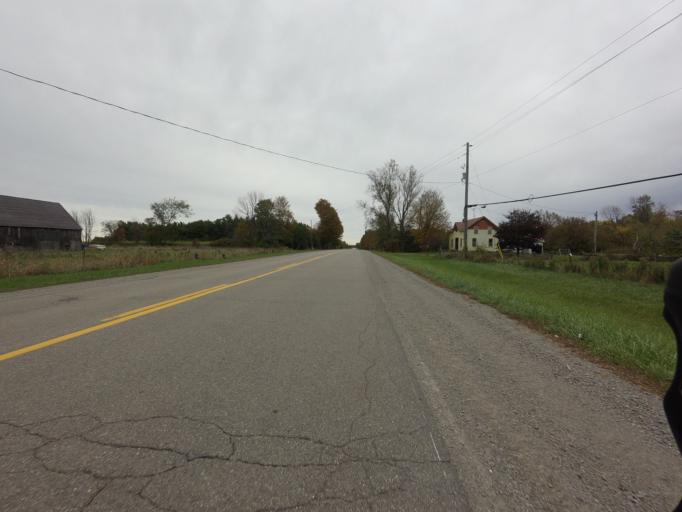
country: CA
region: Ontario
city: Brockville
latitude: 44.6378
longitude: -75.9228
